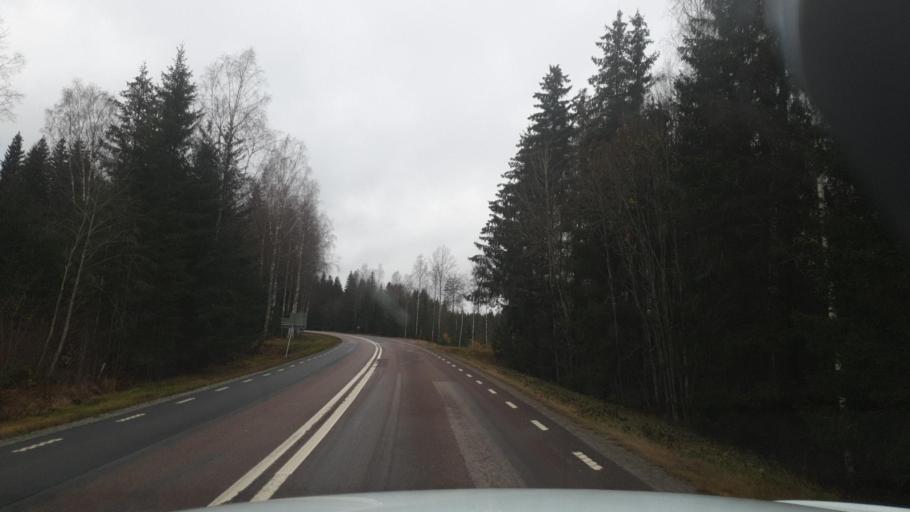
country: SE
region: Vaermland
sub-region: Eda Kommun
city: Amotfors
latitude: 59.6799
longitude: 12.4049
